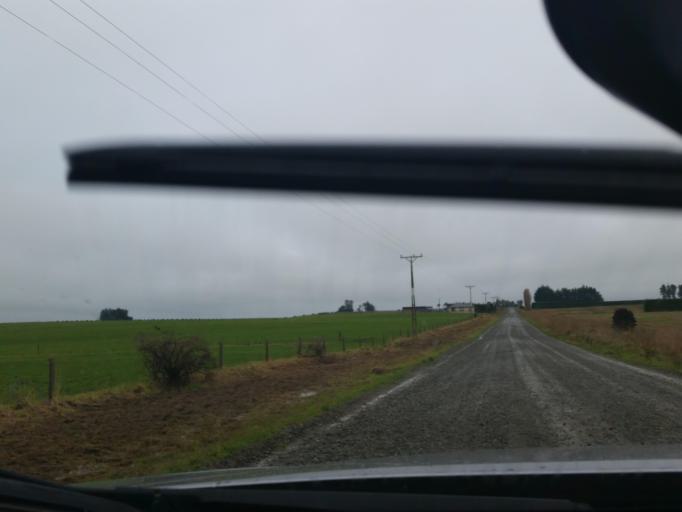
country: NZ
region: Southland
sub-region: Southland District
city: Winton
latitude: -46.1979
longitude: 168.2620
